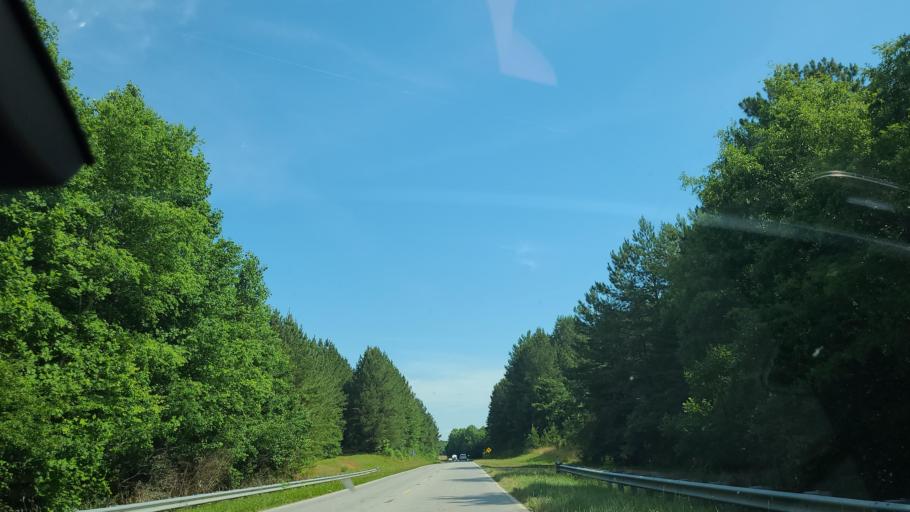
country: US
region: South Carolina
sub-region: Oconee County
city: Westminster
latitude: 34.6818
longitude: -83.0423
